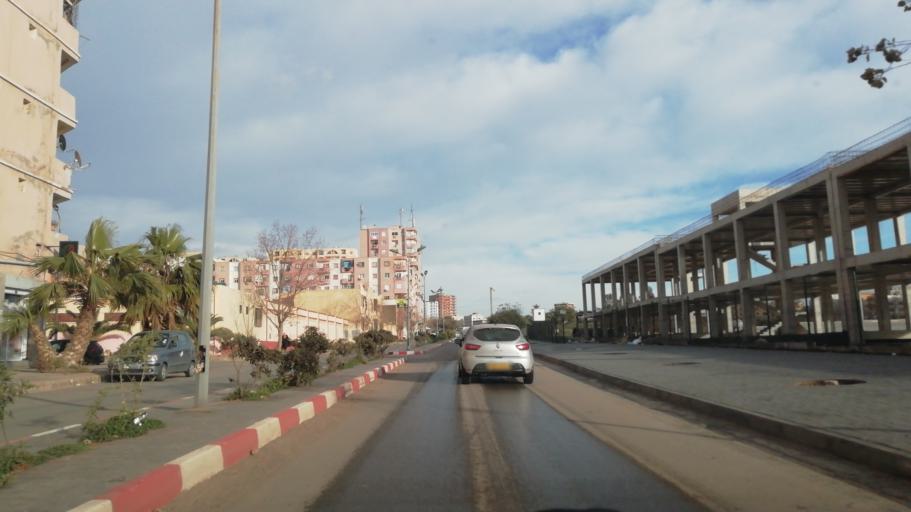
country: DZ
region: Oran
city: Bir el Djir
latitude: 35.7209
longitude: -0.5910
